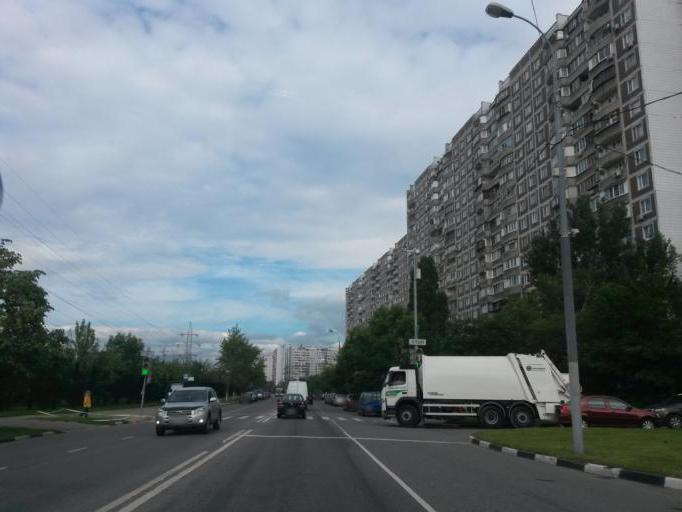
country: RU
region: Moscow
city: Mar'ino
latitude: 55.6433
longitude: 37.7354
